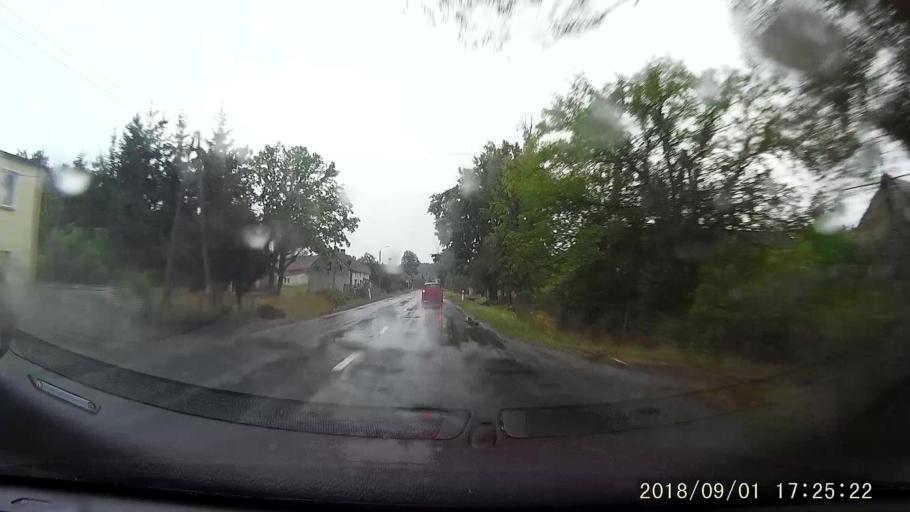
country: PL
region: Lubusz
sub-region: Powiat zaganski
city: Zagan
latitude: 51.6867
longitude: 15.3081
